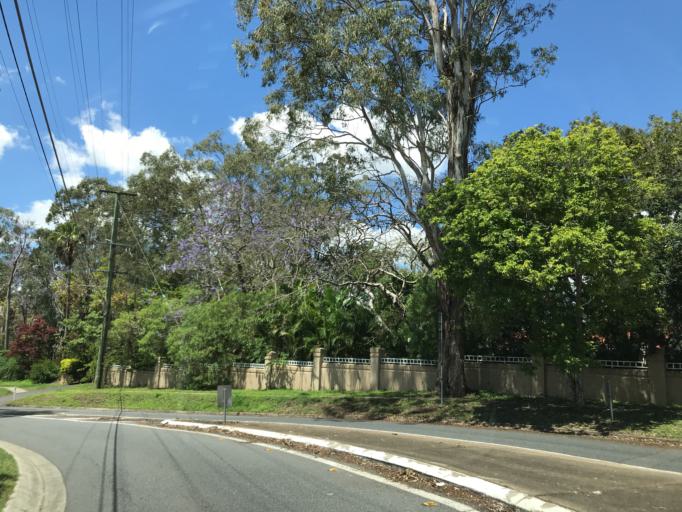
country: AU
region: Queensland
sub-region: Brisbane
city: Kenmore Hills
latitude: -27.5227
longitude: 152.9426
